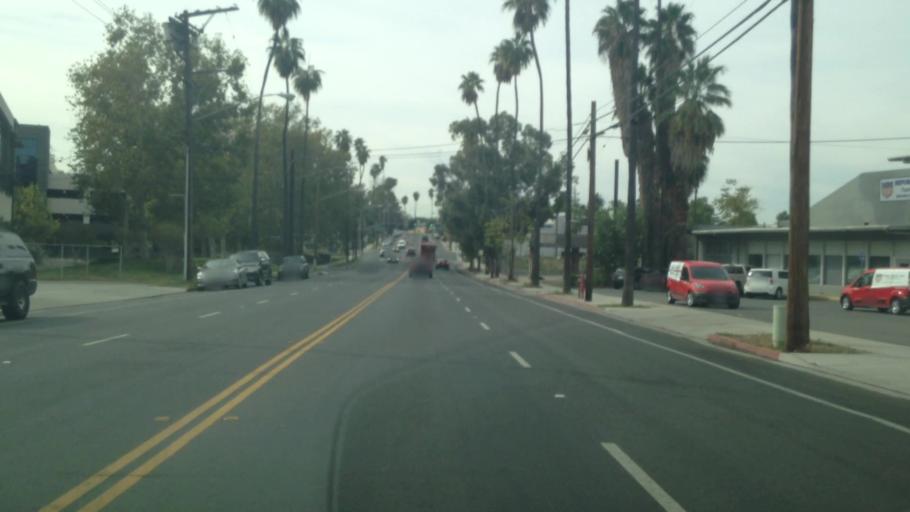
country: US
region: California
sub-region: Riverside County
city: Riverside
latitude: 33.9777
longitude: -117.3840
